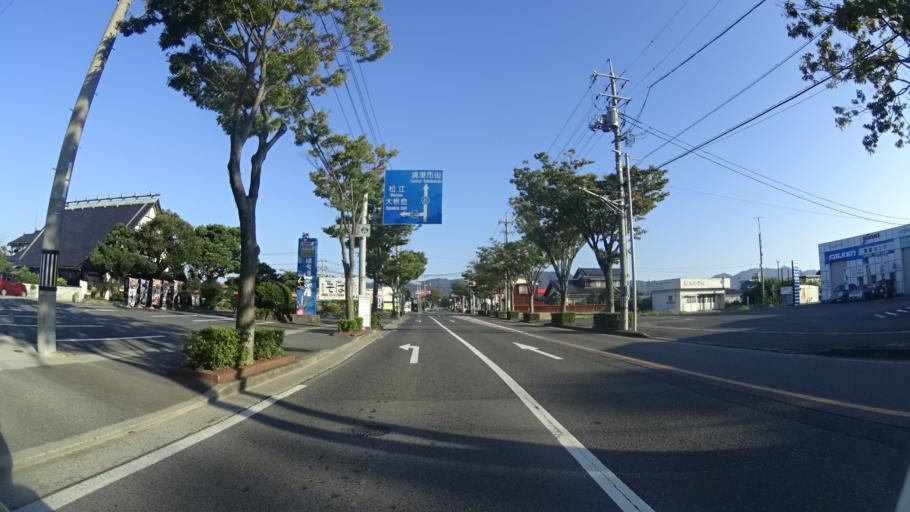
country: JP
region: Shimane
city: Sakaiminato
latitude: 35.5214
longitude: 133.2137
